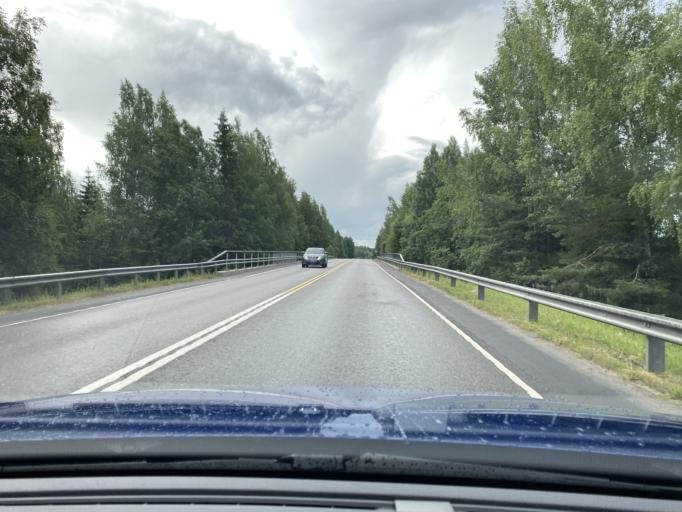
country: FI
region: Uusimaa
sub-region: Helsinki
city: Hyvinge
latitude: 60.5727
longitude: 24.8010
